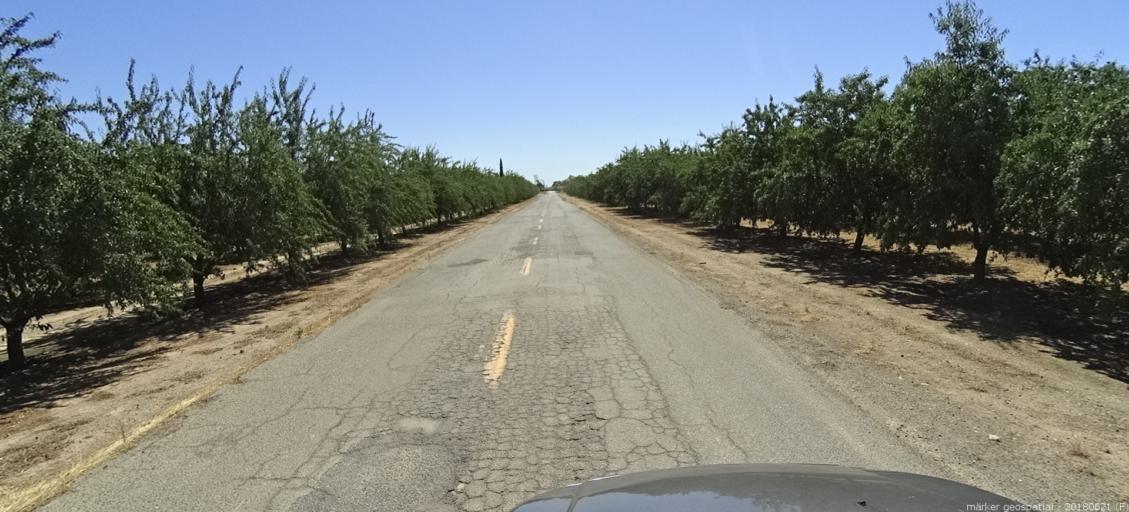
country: US
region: California
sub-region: Madera County
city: Parksdale
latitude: 36.9094
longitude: -119.9684
